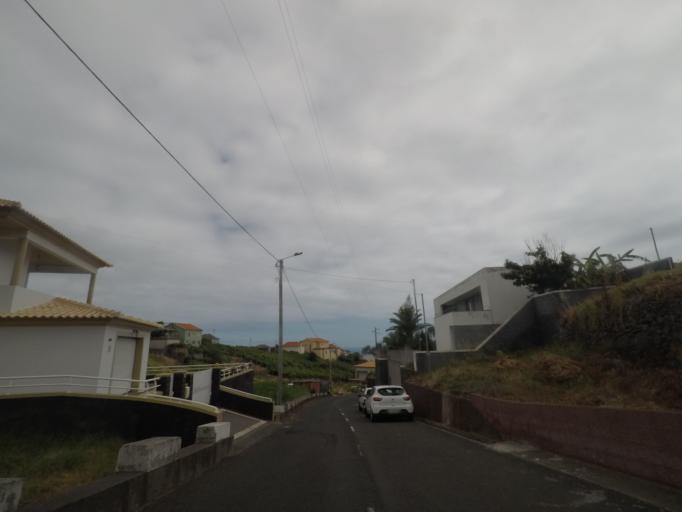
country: PT
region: Madeira
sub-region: Calheta
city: Estreito da Calheta
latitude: 32.7355
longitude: -17.1727
